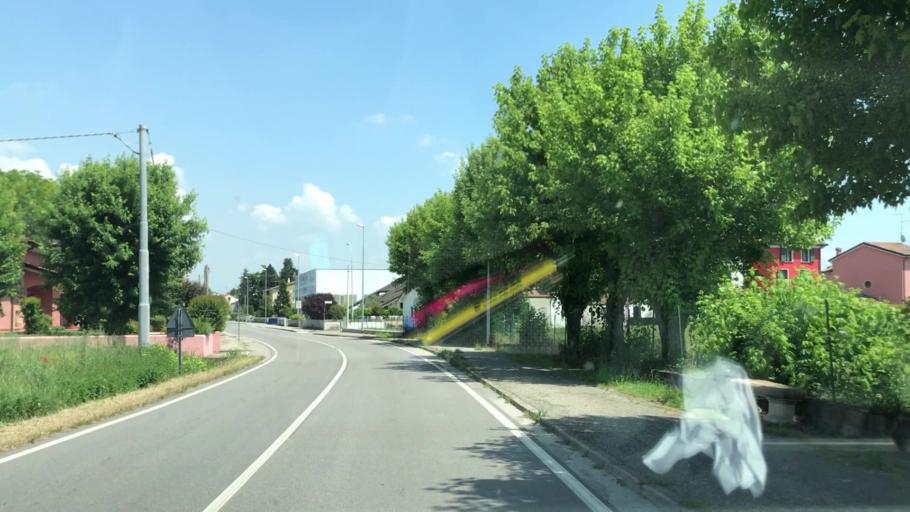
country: IT
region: Lombardy
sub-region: Provincia di Mantova
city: Dosolo
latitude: 45.0167
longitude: 10.6216
